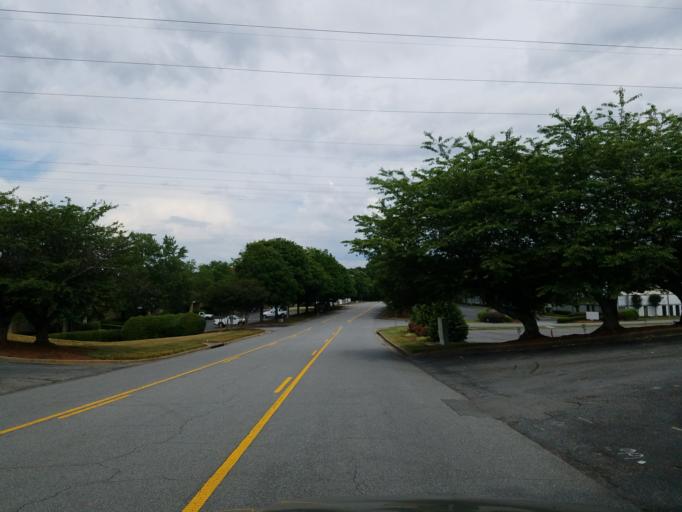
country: US
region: Georgia
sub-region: Cobb County
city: Smyrna
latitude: 33.9184
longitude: -84.4908
